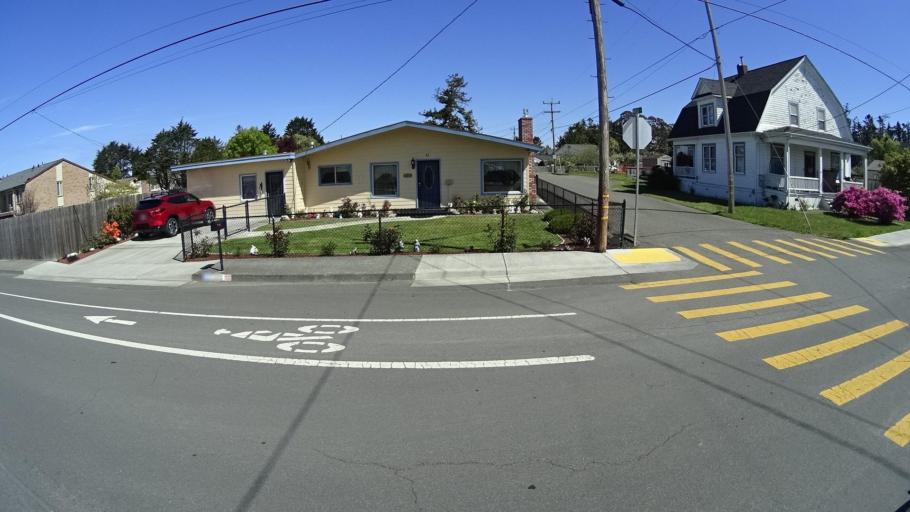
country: US
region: California
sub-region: Humboldt County
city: Myrtletown
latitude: 40.7950
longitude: -124.1304
